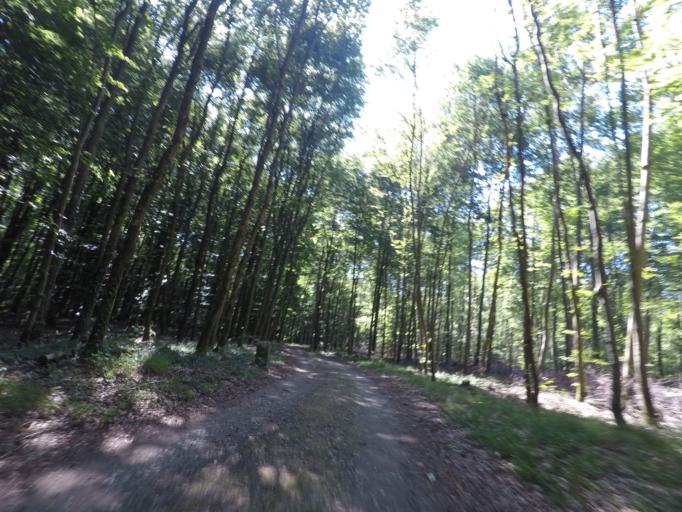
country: LU
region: Luxembourg
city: Bridel
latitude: 49.6425
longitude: 6.0772
